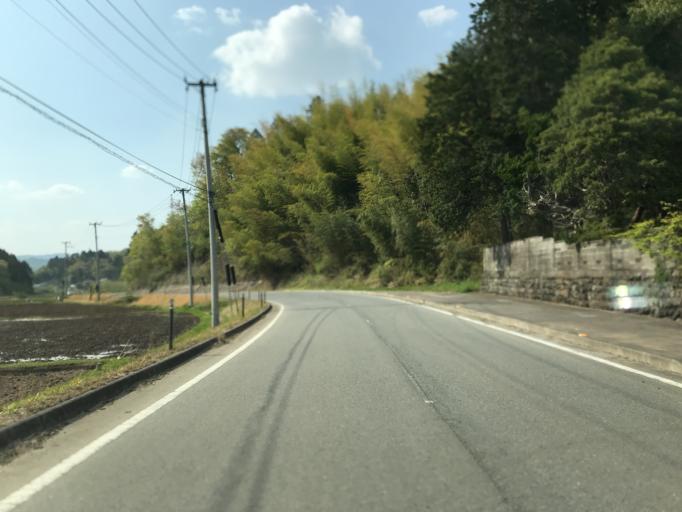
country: JP
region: Fukushima
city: Iwaki
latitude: 37.0029
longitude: 140.7671
